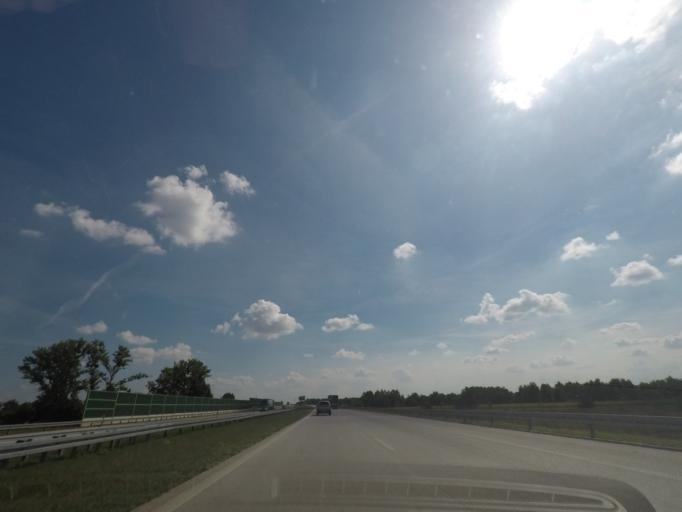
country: PL
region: Lodz Voivodeship
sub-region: Powiat lodzki wschodni
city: Andrespol
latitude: 51.7601
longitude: 19.5954
